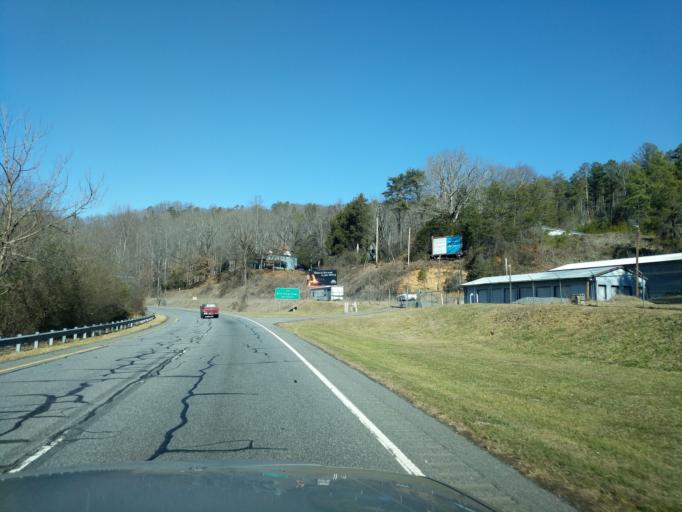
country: US
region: North Carolina
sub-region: Swain County
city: Cherokee
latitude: 35.4142
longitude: -83.3267
